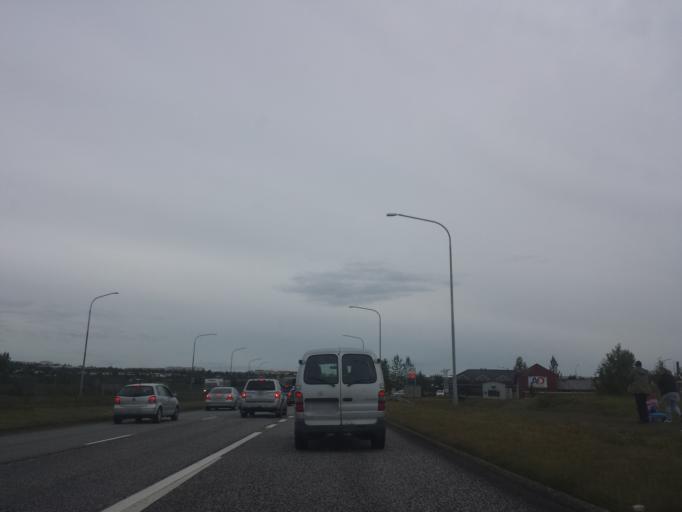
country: IS
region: Capital Region
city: Reykjavik
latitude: 64.1223
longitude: -21.8479
